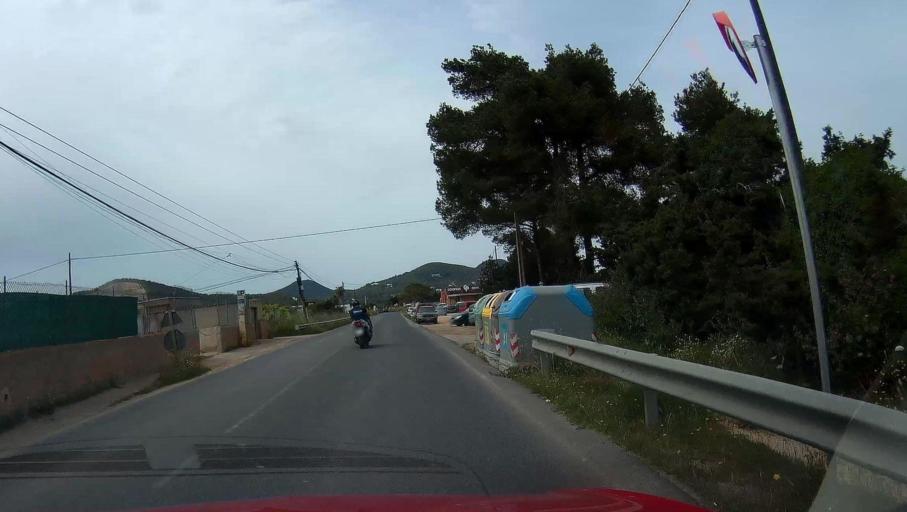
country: ES
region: Balearic Islands
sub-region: Illes Balears
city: Ibiza
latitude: 38.8776
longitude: 1.3641
